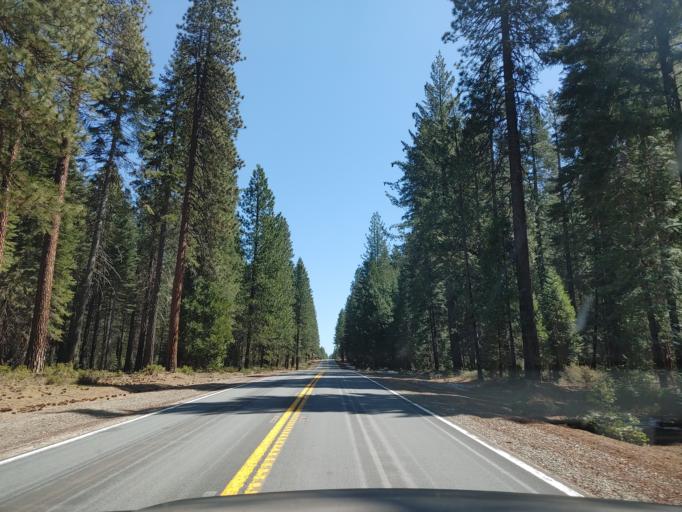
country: US
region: California
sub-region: Siskiyou County
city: McCloud
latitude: 41.2677
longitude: -121.9124
